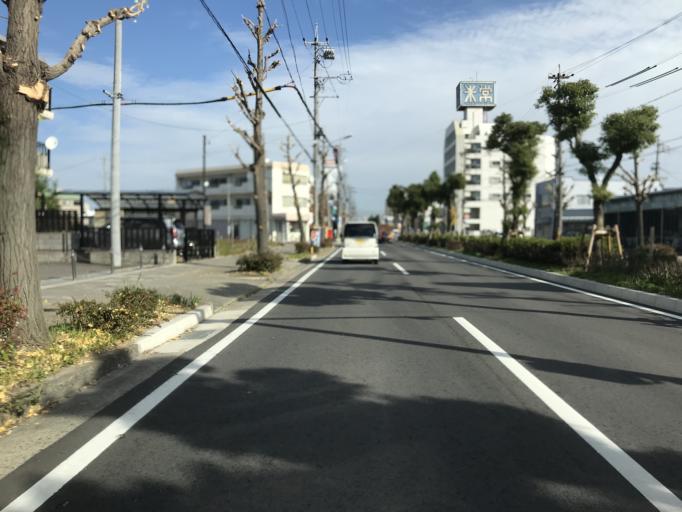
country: JP
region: Aichi
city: Nagoya-shi
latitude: 35.1997
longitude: 136.9180
